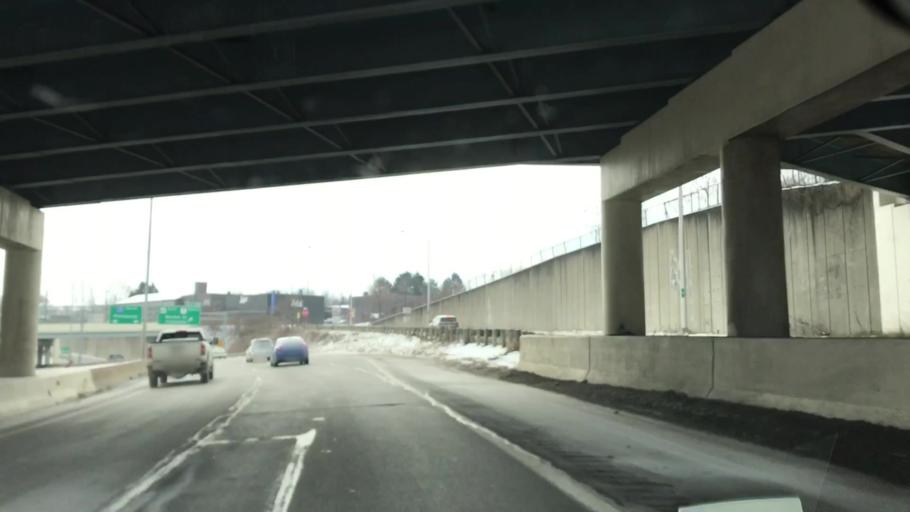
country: US
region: Ohio
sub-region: Mahoning County
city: Youngstown
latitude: 41.0938
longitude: -80.6562
